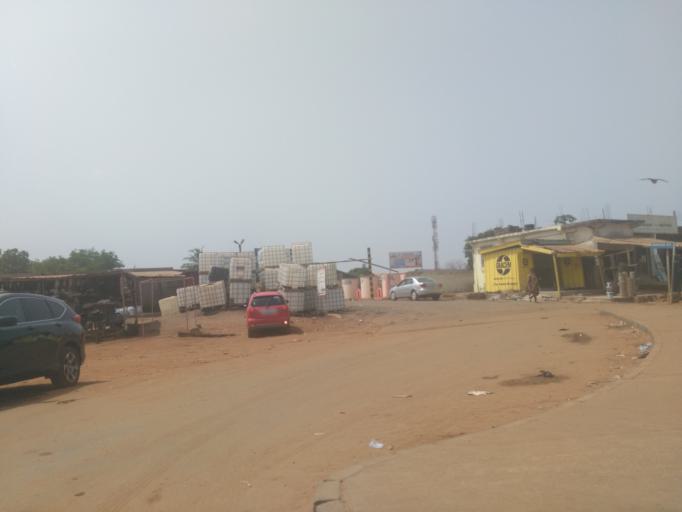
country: GH
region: Greater Accra
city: Tema
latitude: 5.6961
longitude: -0.0137
